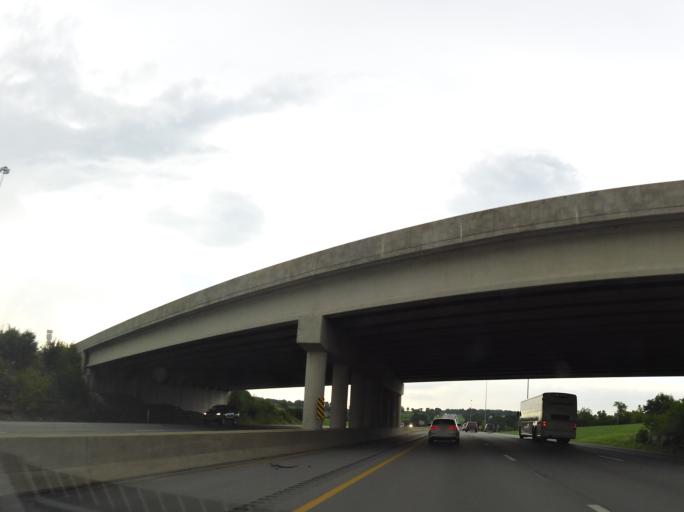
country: US
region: Kentucky
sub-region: Fayette County
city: Lexington
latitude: 37.9622
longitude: -84.3887
